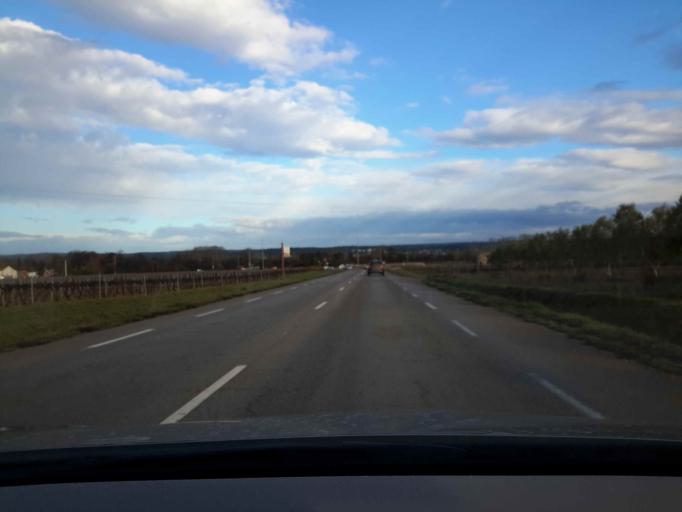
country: FR
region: Languedoc-Roussillon
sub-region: Departement du Gard
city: Aubord
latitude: 43.7672
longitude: 4.3290
